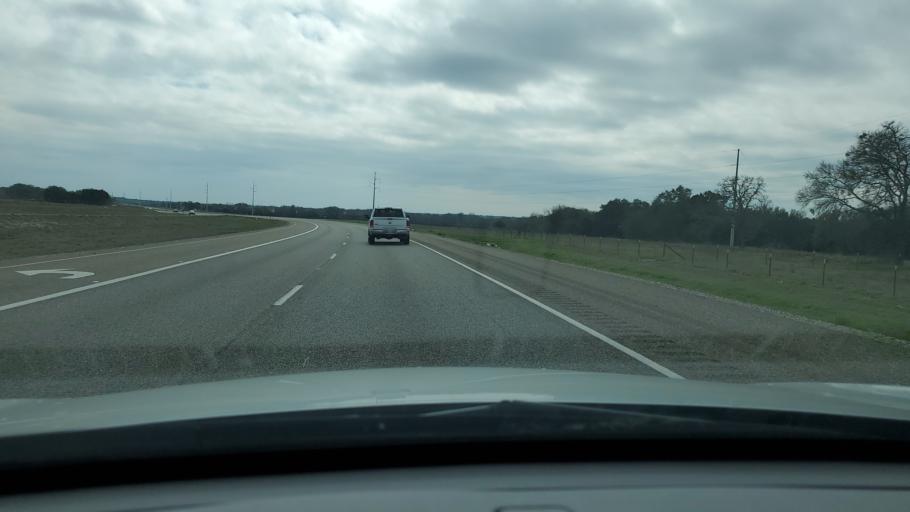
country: US
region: Texas
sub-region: Williamson County
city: Florence
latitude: 30.7727
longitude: -97.7585
